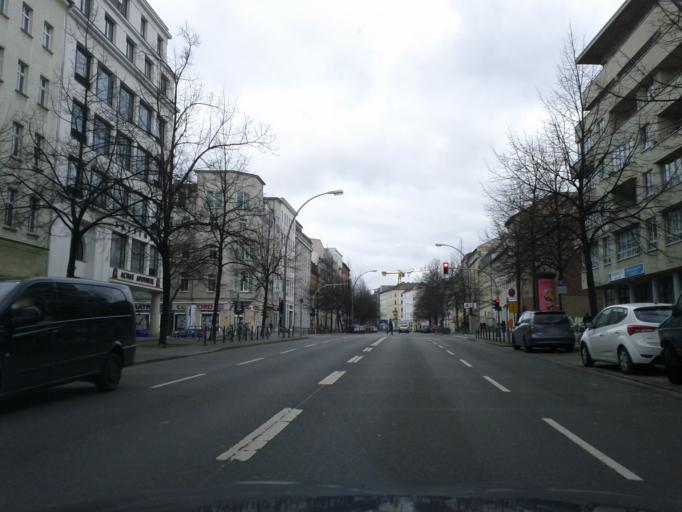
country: DE
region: Berlin
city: Berlin
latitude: 52.5345
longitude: 13.3983
